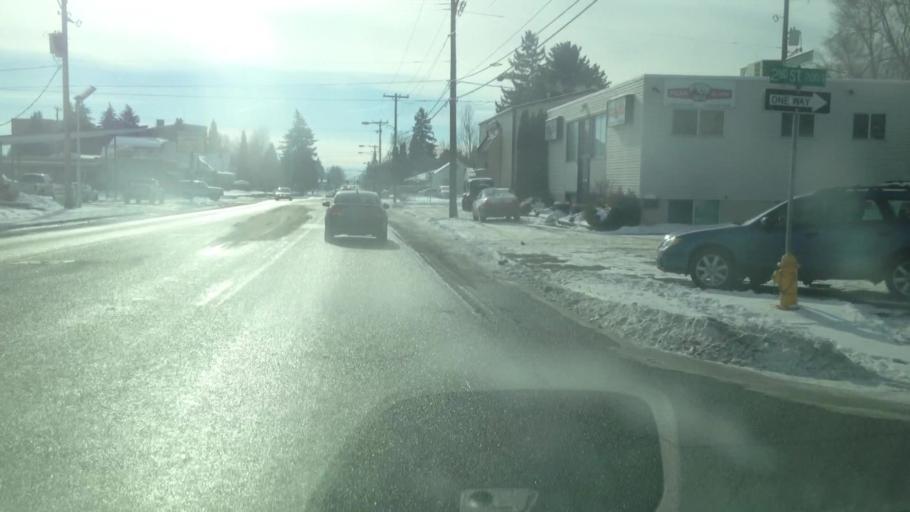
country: US
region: Idaho
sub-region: Bonneville County
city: Idaho Falls
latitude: 43.4961
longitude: -112.0239
